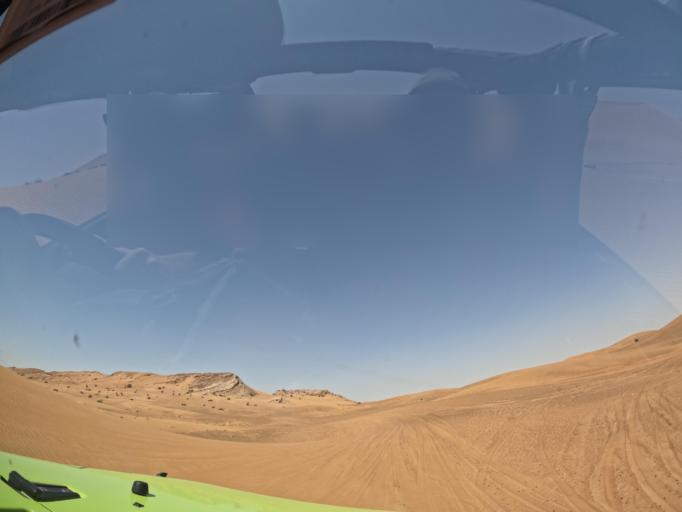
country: AE
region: Ash Shariqah
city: Adh Dhayd
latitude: 25.0204
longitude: 55.7363
